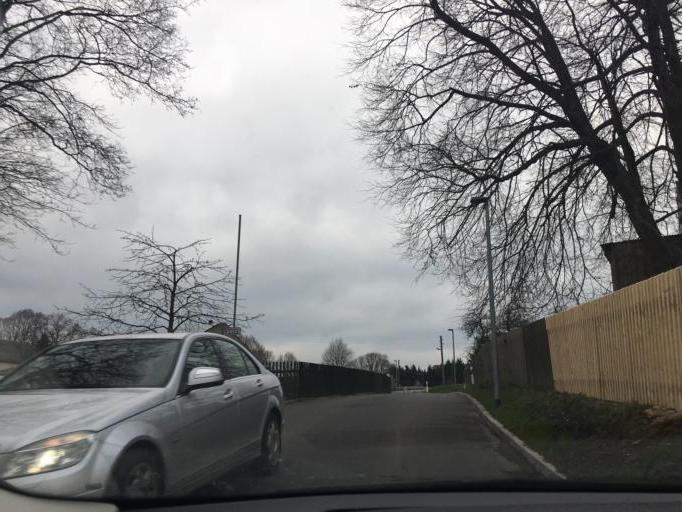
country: DE
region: Saxony
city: Niederfrohna
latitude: 50.8734
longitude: 12.7068
